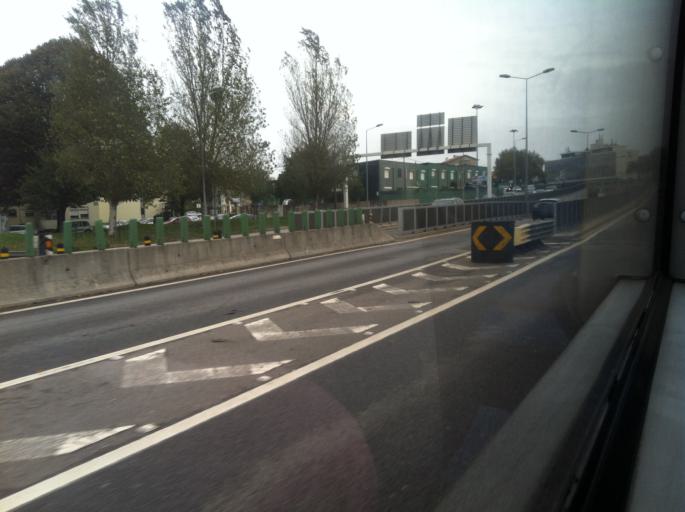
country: PT
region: Porto
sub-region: Matosinhos
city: Senhora da Hora
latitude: 41.1663
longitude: -8.6411
